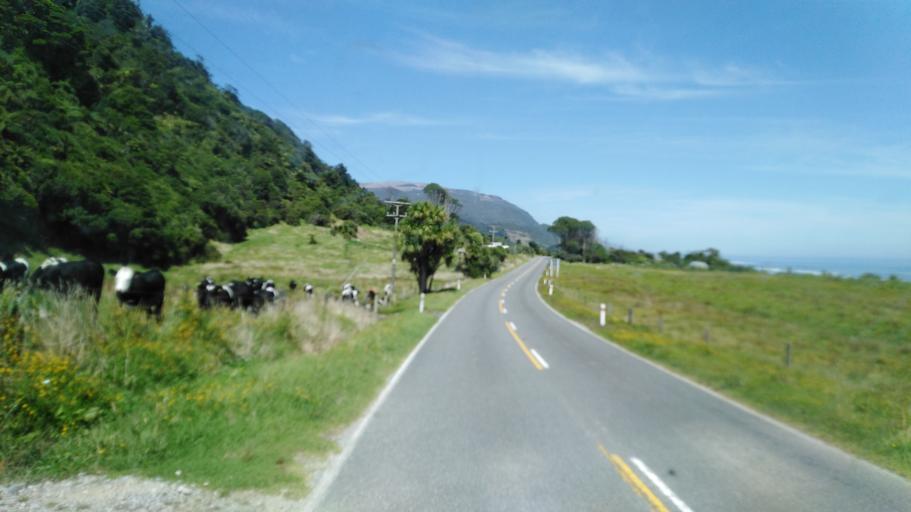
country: NZ
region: West Coast
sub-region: Buller District
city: Westport
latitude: -41.5930
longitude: 171.8895
